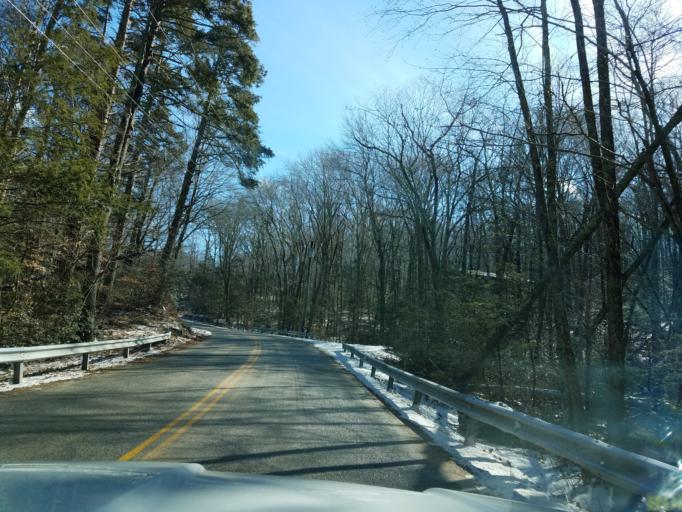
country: US
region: Connecticut
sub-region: New London County
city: Preston City
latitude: 41.4645
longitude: -71.9414
